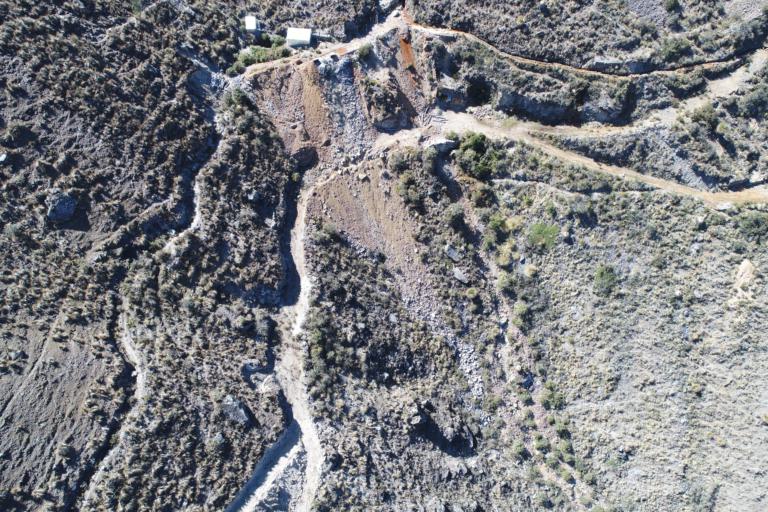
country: BO
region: La Paz
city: Viloco
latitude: -16.8074
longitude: -67.5540
